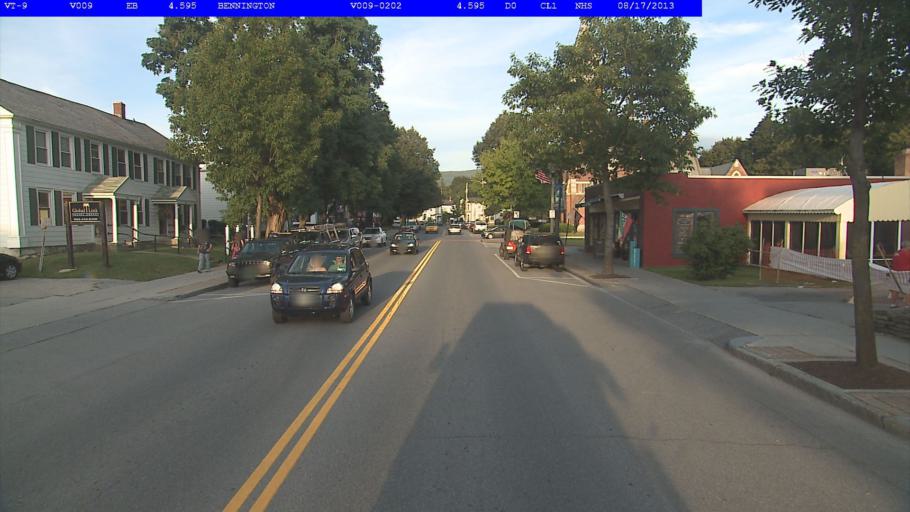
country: US
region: Vermont
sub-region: Bennington County
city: Bennington
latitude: 42.8780
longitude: -73.1933
